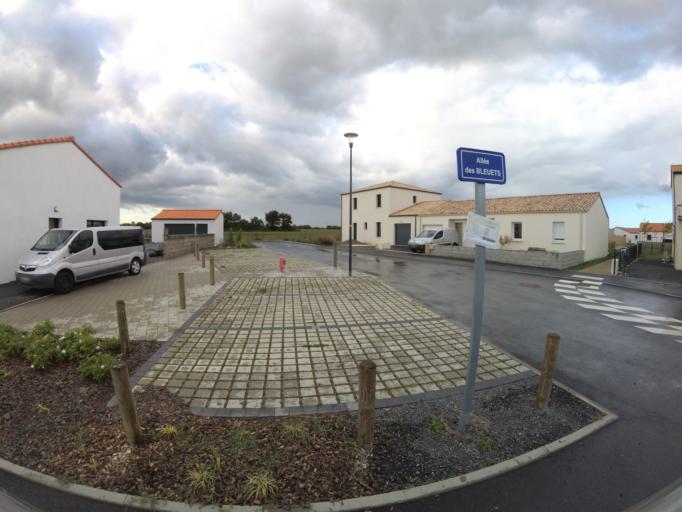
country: FR
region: Pays de la Loire
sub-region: Departement de la Loire-Atlantique
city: Saint-Lumine-de-Clisson
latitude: 47.0876
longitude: -1.3349
